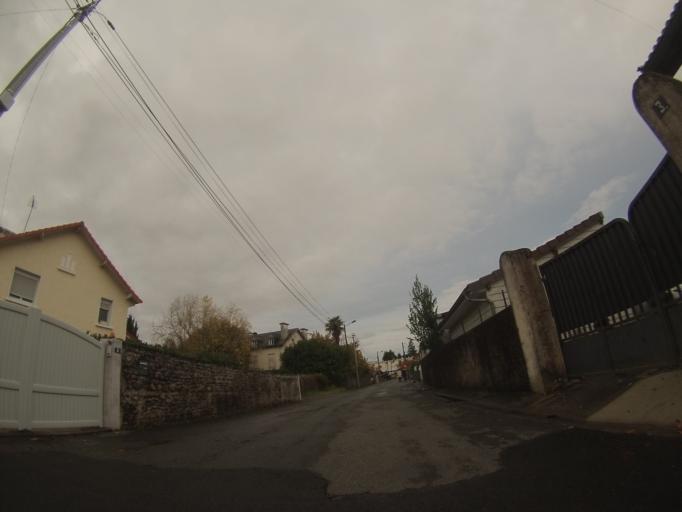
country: FR
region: Aquitaine
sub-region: Departement des Pyrenees-Atlantiques
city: Jurancon
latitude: 43.2810
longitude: -0.3884
